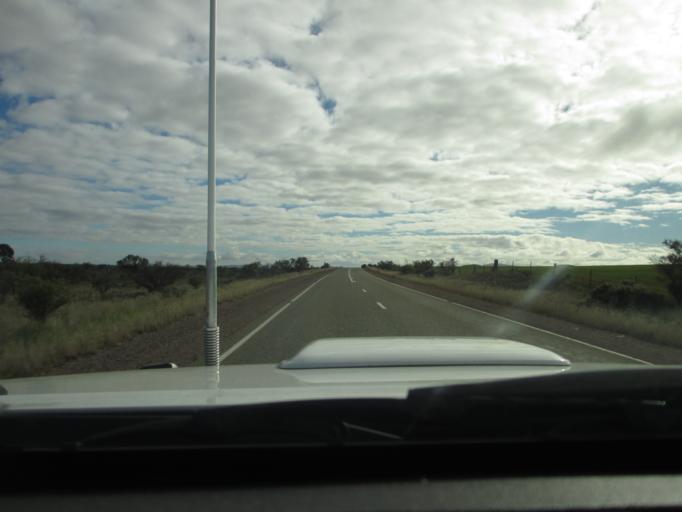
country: AU
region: South Australia
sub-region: Flinders Ranges
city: Quorn
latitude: -32.4517
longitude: 138.5367
